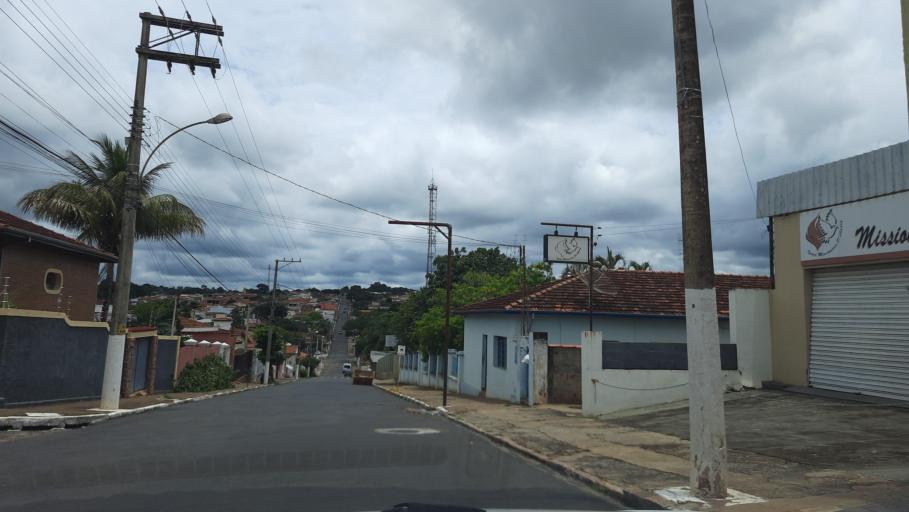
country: BR
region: Sao Paulo
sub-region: Casa Branca
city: Casa Branca
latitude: -21.7759
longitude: -47.0882
